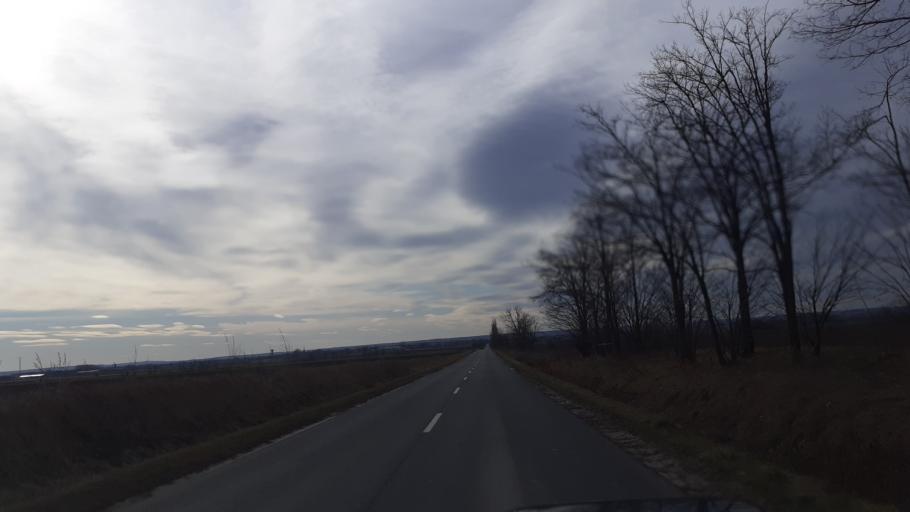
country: HU
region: Fejer
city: Sarbogard
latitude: 46.9060
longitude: 18.6553
